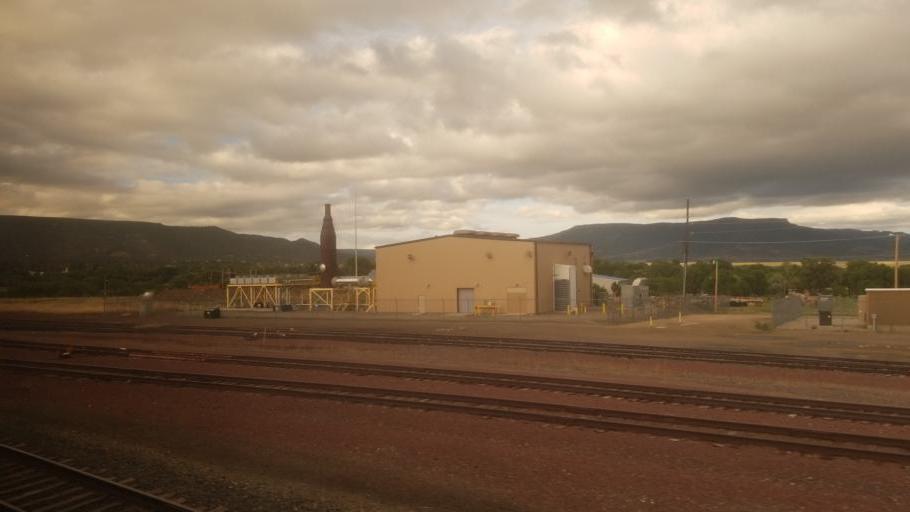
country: US
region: New Mexico
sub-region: Colfax County
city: Raton
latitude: 36.8935
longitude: -104.4392
